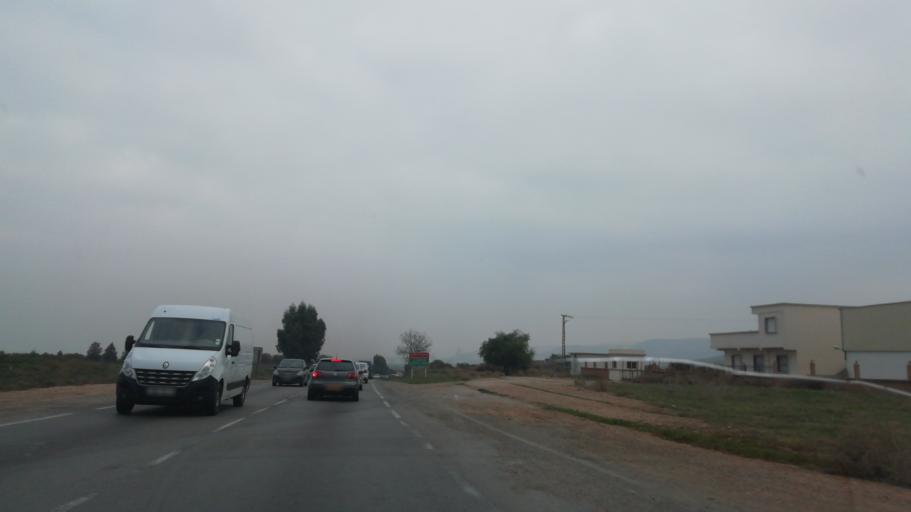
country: DZ
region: Mascara
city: Sig
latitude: 35.5390
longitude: -0.3477
